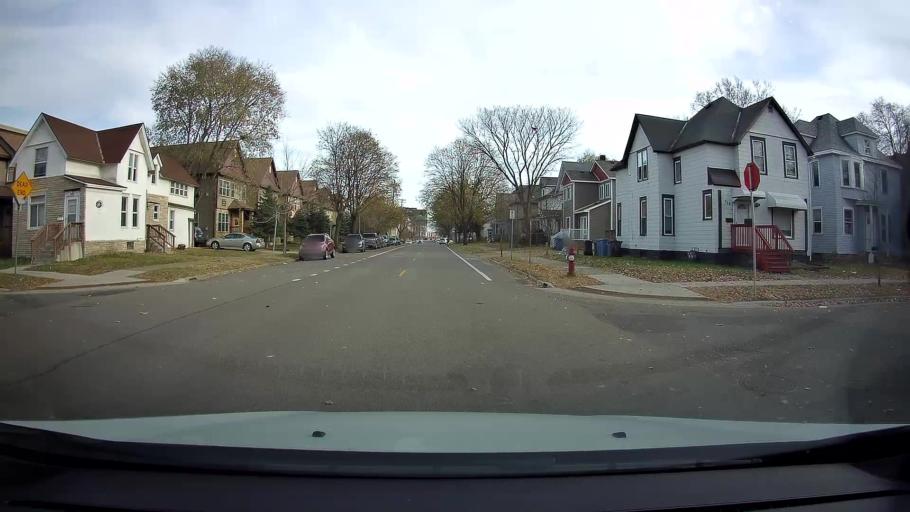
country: US
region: Minnesota
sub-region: Hennepin County
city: Minneapolis
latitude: 44.9850
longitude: -93.2341
